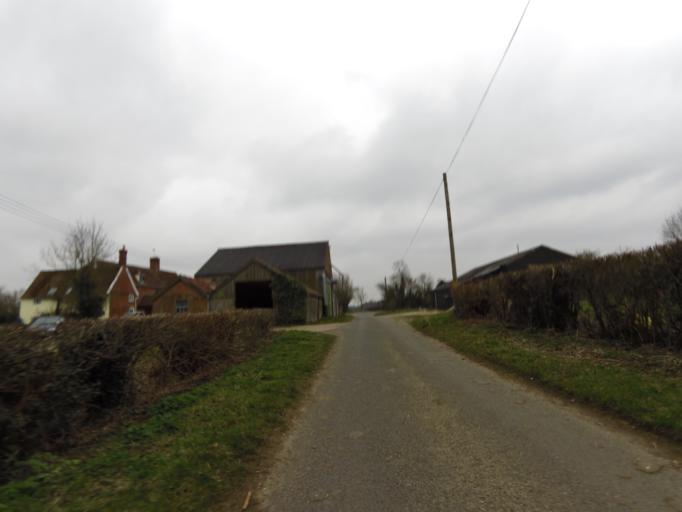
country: GB
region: England
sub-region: Suffolk
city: Framlingham
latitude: 52.2170
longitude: 1.3277
